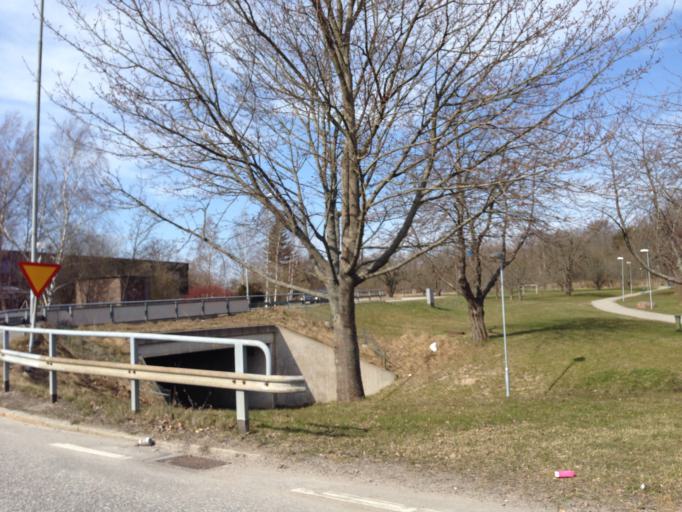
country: SE
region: Stockholm
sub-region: Botkyrka Kommun
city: Eriksberg
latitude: 59.2501
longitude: 17.8310
